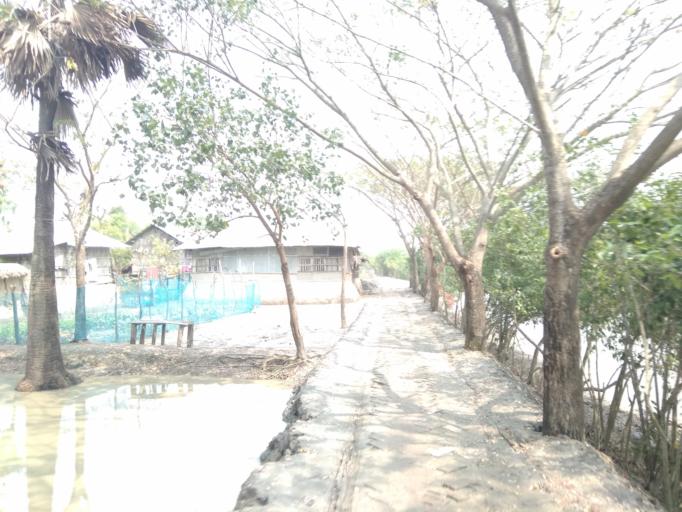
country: IN
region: West Bengal
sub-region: North 24 Parganas
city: Taki
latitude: 22.2583
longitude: 89.2584
